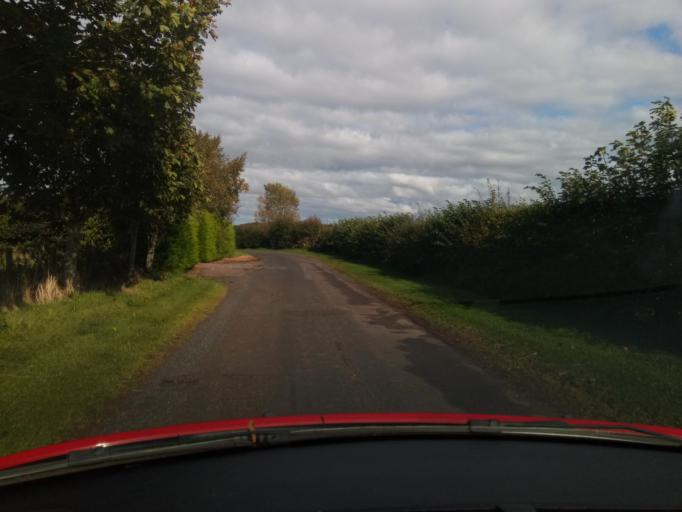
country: GB
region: Scotland
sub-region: The Scottish Borders
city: Kelso
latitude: 55.5725
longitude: -2.4079
